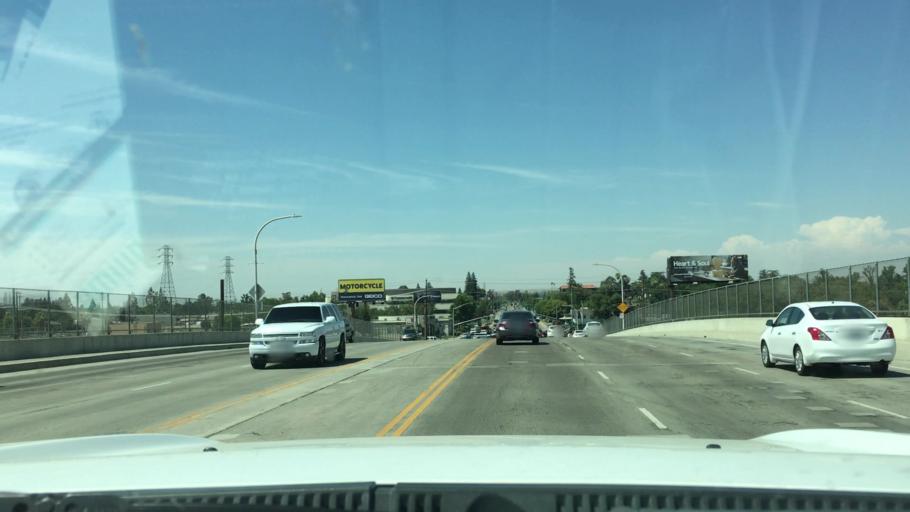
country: US
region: California
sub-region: Kern County
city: Bakersfield
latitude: 35.3713
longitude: -119.0387
